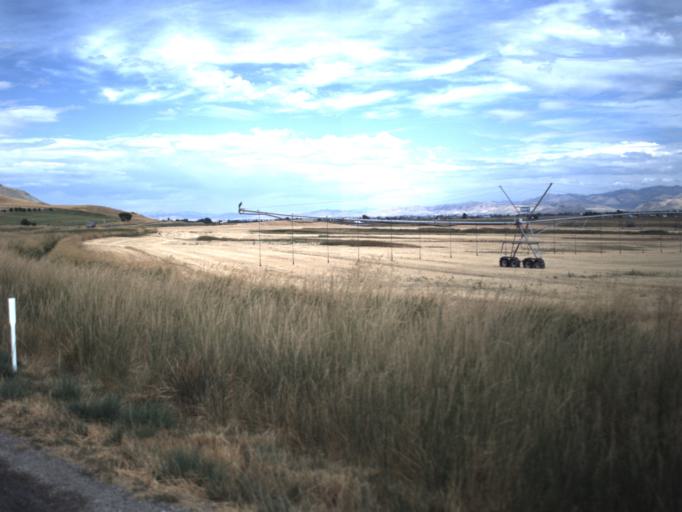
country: US
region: Utah
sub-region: Cache County
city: Benson
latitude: 41.8812
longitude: -111.9514
